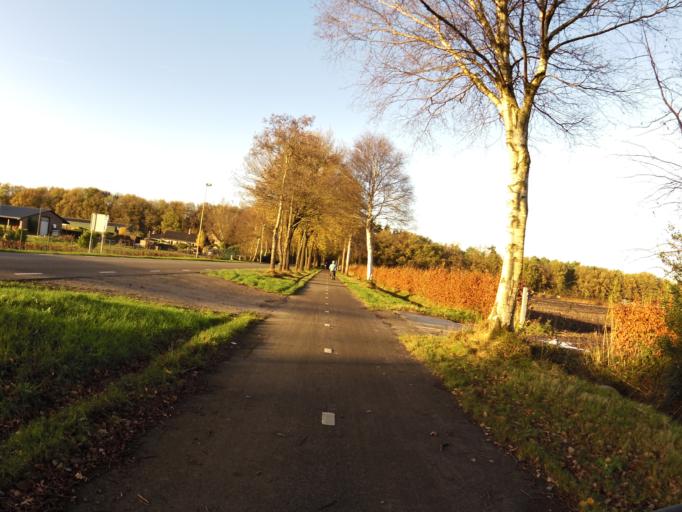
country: NL
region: North Brabant
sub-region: Gemeente Heusden
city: Heusden
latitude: 51.6637
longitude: 5.1454
